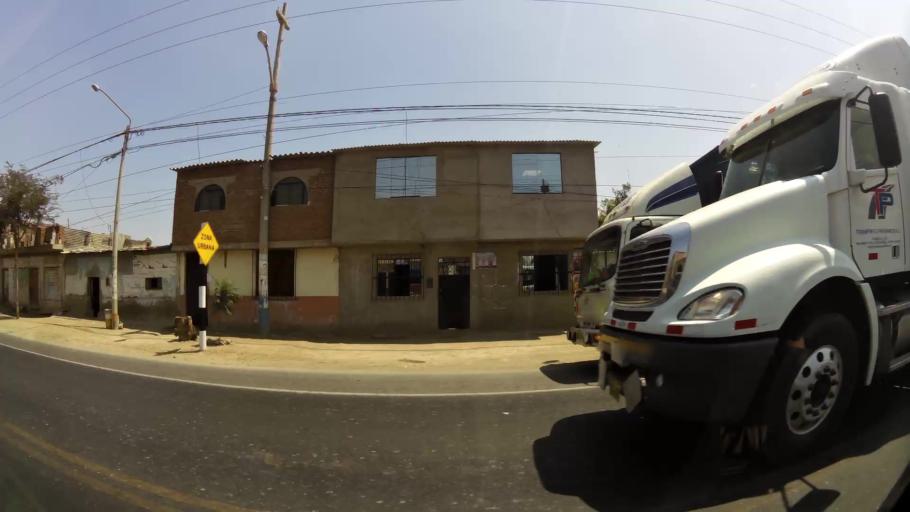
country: PE
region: La Libertad
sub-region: Chepen
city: Chepen
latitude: -7.2057
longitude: -79.4274
